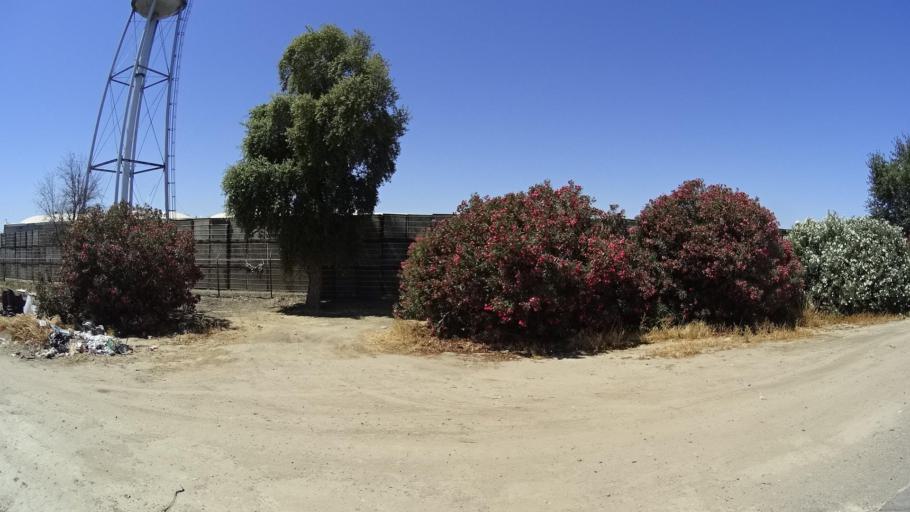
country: US
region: California
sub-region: Fresno County
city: Fresno
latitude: 36.6998
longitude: -119.7611
